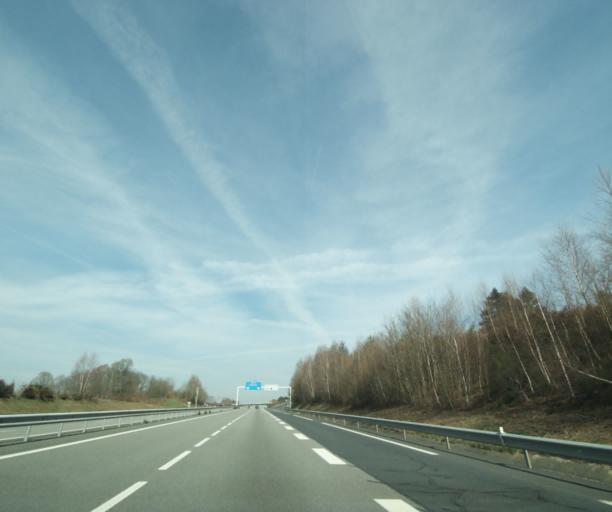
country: FR
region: Limousin
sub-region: Departement de la Correze
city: Saint-Mexant
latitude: 45.3159
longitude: 1.5747
